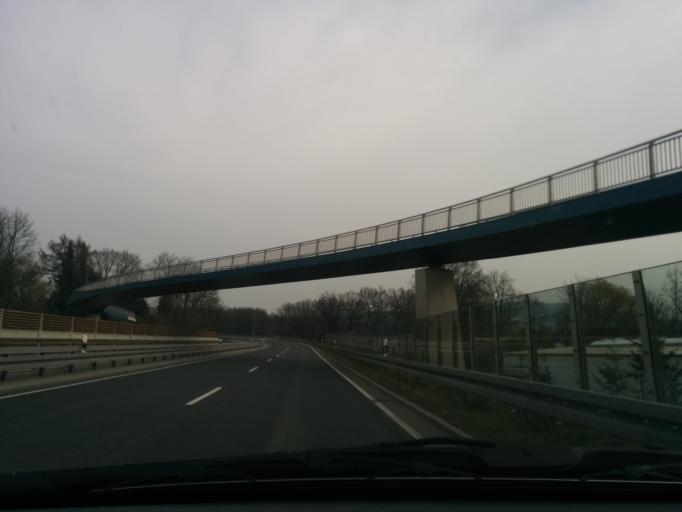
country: DE
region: Saxony
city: Floha
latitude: 50.8513
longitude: 13.0791
